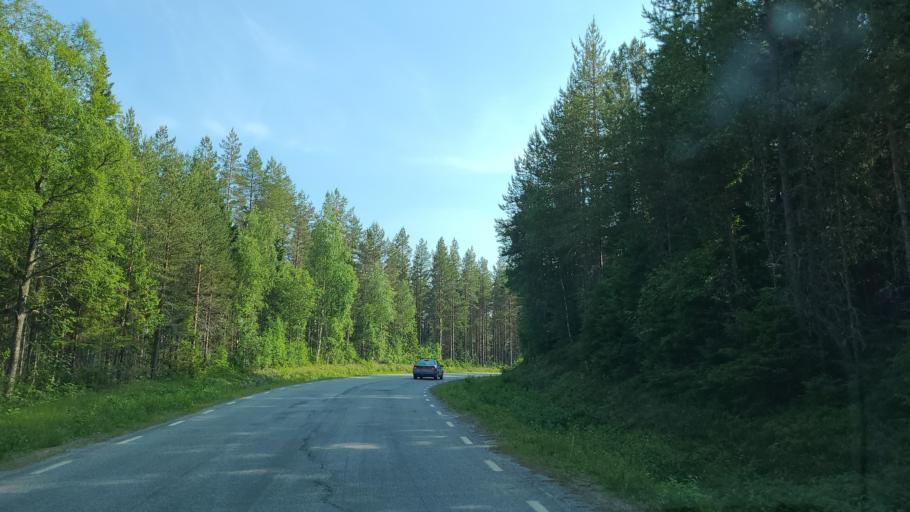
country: SE
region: Vaesterbotten
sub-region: Skelleftea Kommun
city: Burea
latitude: 64.3555
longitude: 21.3380
